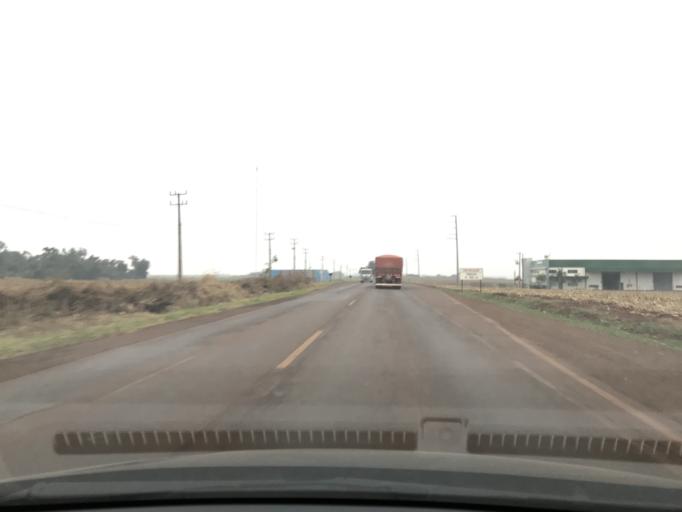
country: BR
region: Parana
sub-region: Palotina
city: Palotina
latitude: -24.3144
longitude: -53.8332
